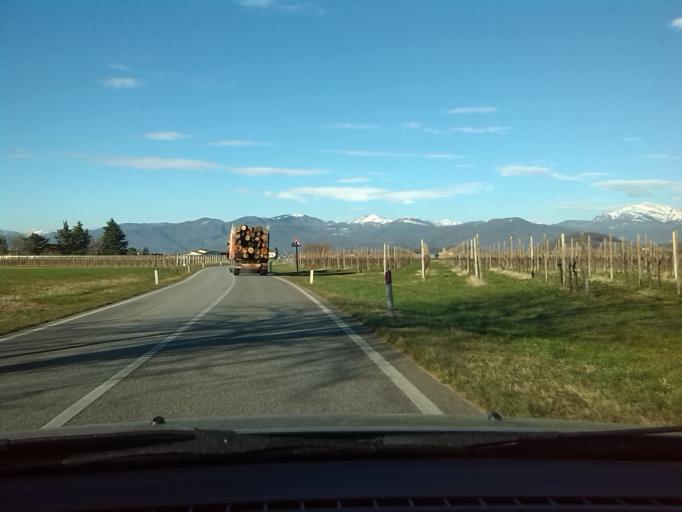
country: IT
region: Friuli Venezia Giulia
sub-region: Provincia di Udine
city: Cividale del Friuli
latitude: 46.0577
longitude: 13.4355
